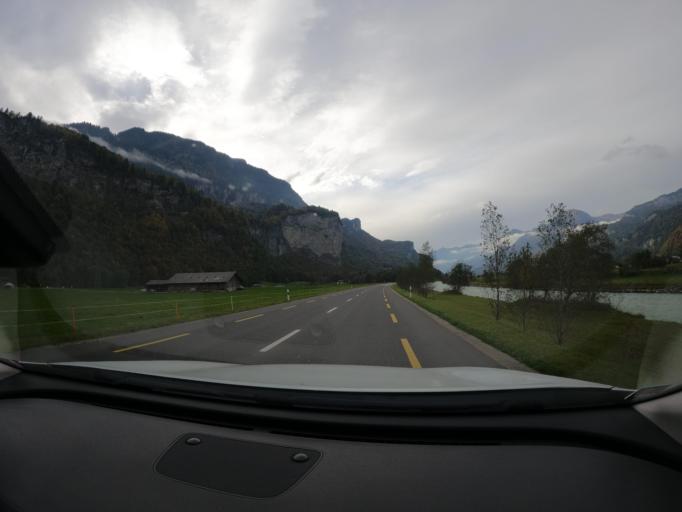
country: CH
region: Bern
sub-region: Interlaken-Oberhasli District
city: Meiringen
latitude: 46.7224
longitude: 8.1843
